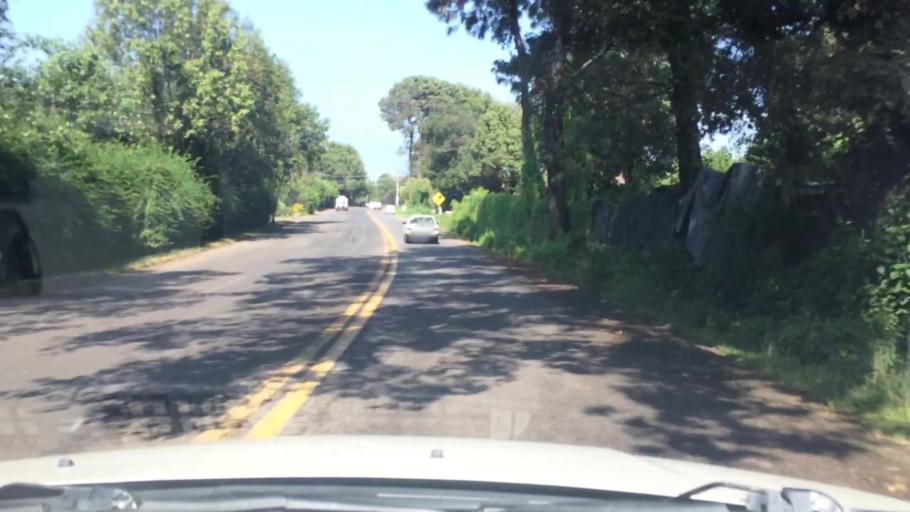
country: MX
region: Mexico
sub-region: Valle de Bravo
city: Casas Viejas
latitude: 19.1592
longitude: -100.0988
